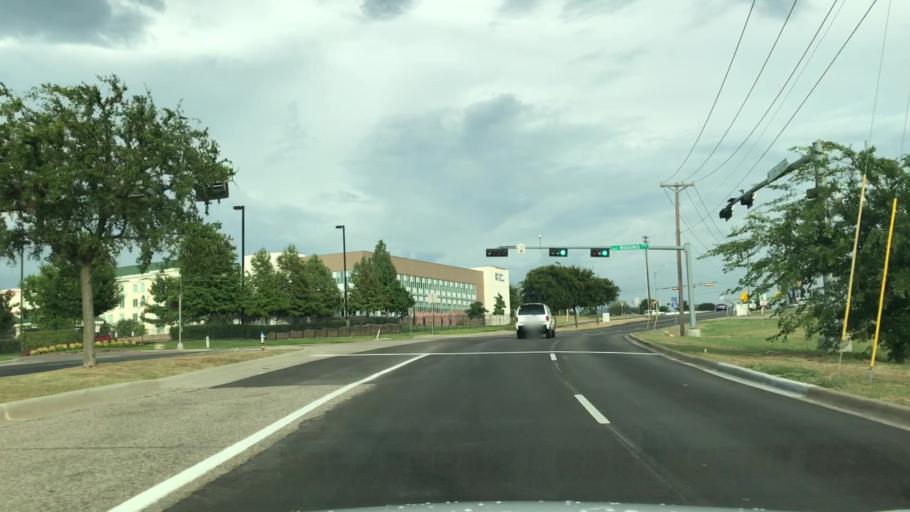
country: US
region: Texas
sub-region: Dallas County
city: Sunnyvale
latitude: 32.8349
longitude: -96.6143
